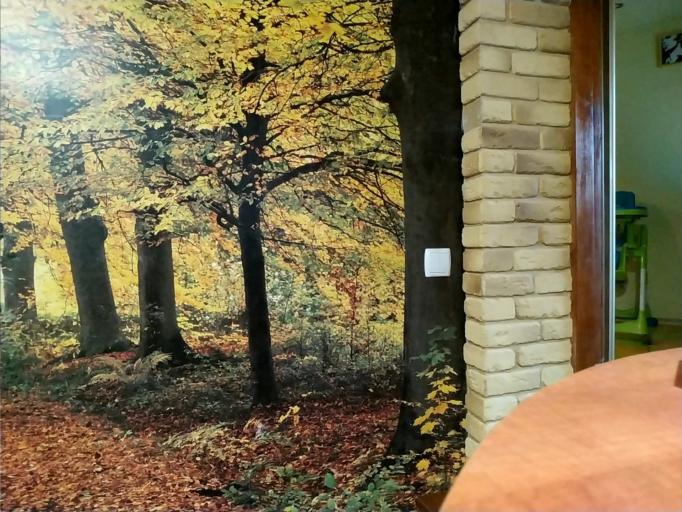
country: BY
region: Minsk
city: Il'ya
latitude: 54.4221
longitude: 27.4658
